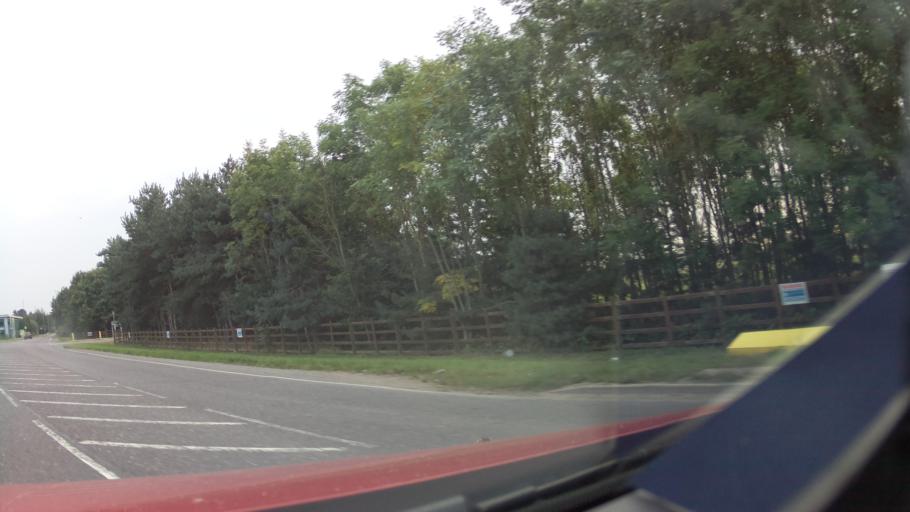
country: GB
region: England
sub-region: Lincolnshire
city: Skellingthorpe
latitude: 53.1542
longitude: -0.6716
